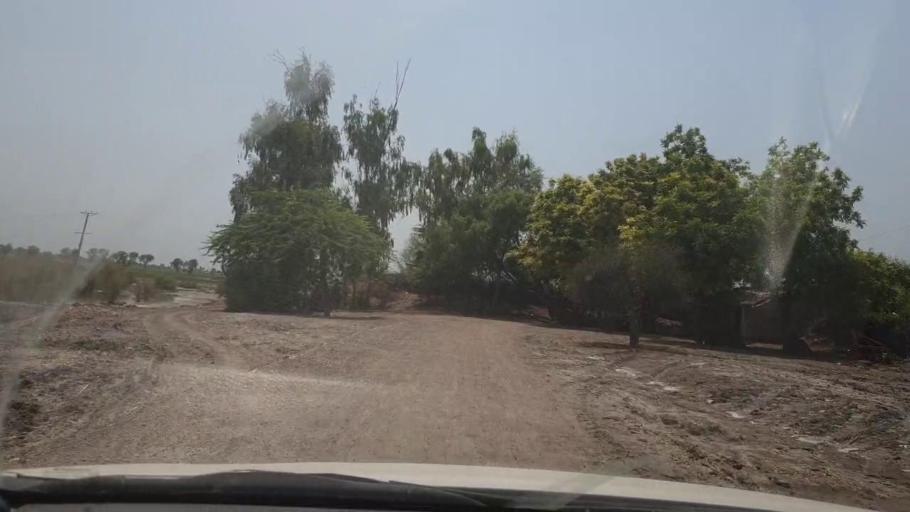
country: PK
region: Sindh
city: Lakhi
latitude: 27.8793
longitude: 68.7461
